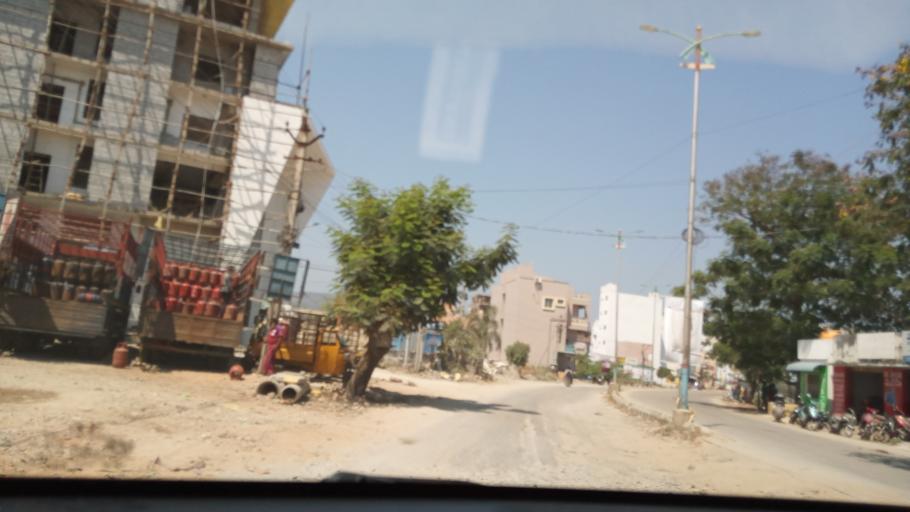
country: IN
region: Andhra Pradesh
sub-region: Chittoor
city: Tirupati
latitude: 13.6105
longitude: 79.4132
